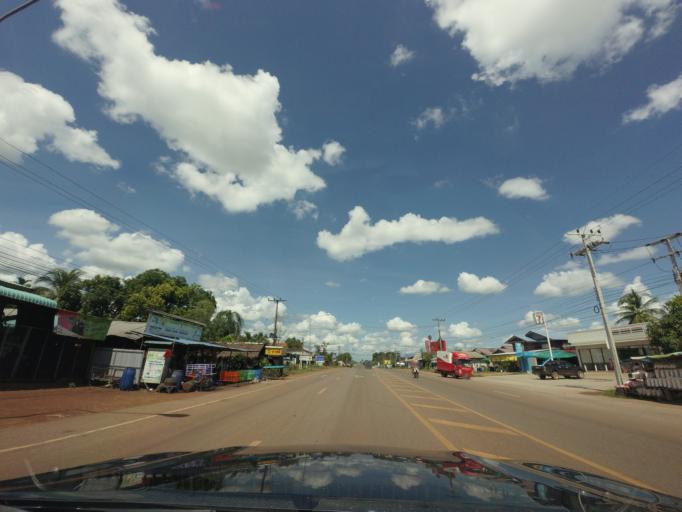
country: TH
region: Changwat Udon Thani
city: Ban Dung
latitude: 17.7454
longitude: 103.2636
